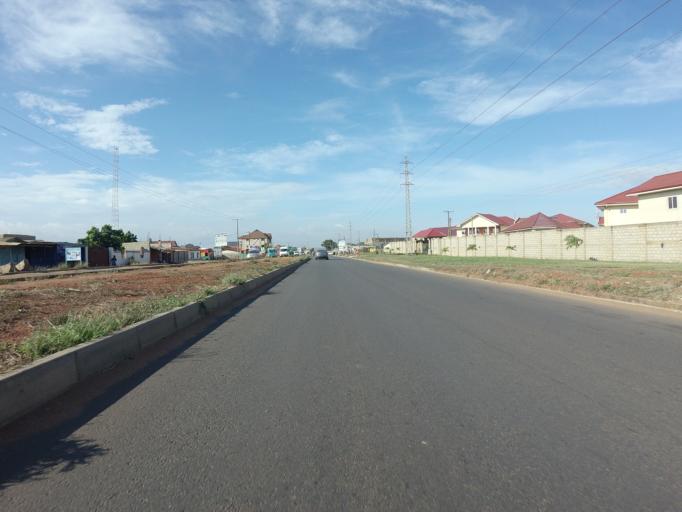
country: GH
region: Greater Accra
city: Nungua
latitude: 5.6361
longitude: -0.0635
